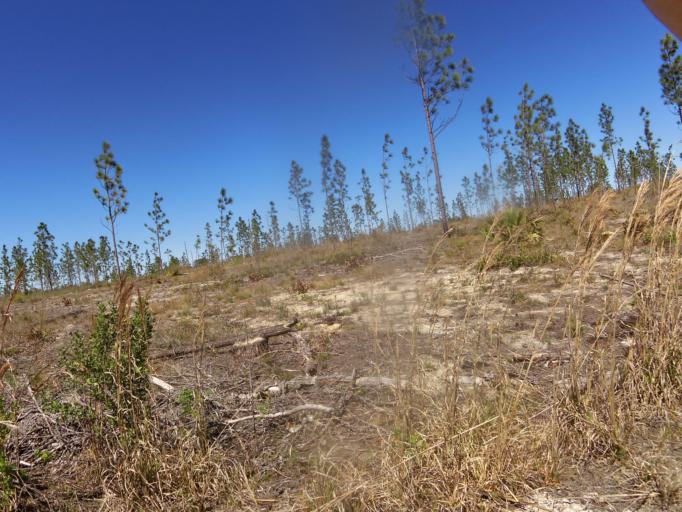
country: US
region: Florida
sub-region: Clay County
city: Keystone Heights
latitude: 29.8366
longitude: -81.9790
